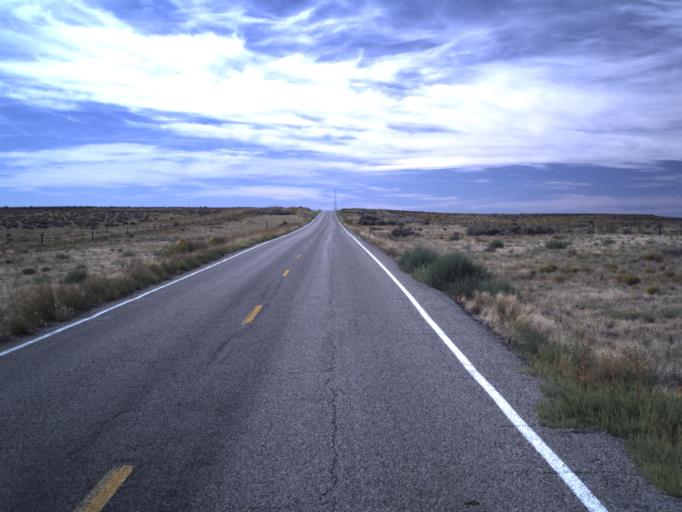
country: US
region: Utah
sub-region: San Juan County
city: Blanding
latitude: 37.3456
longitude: -109.3483
